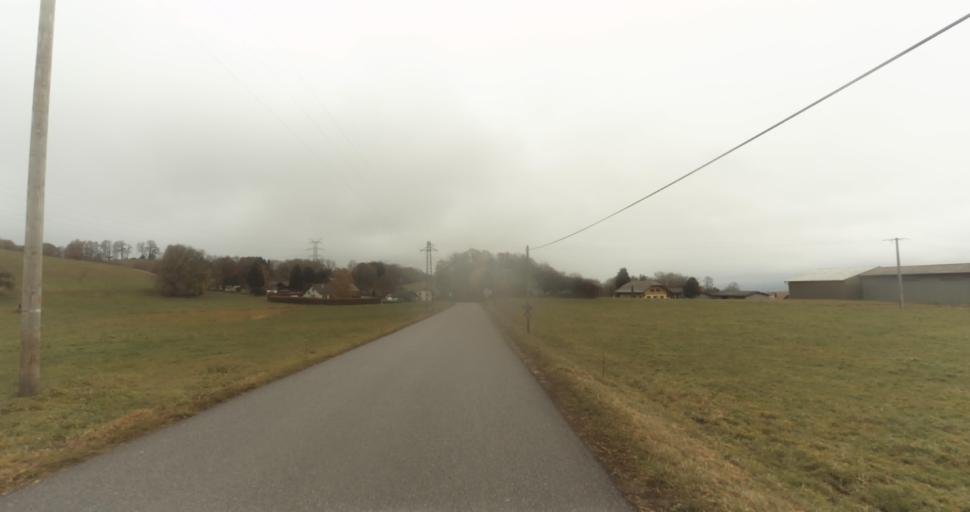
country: FR
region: Rhone-Alpes
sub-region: Departement de la Haute-Savoie
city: Evires
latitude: 46.0521
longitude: 6.2063
